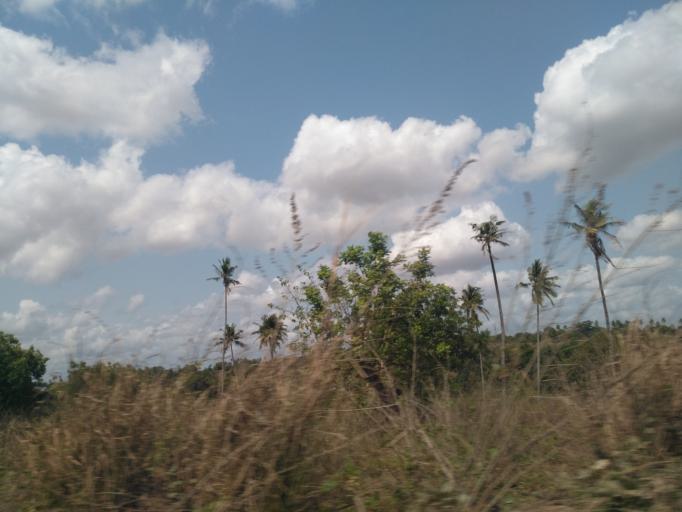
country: TZ
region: Dar es Salaam
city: Dar es Salaam
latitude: -6.8822
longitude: 39.3328
